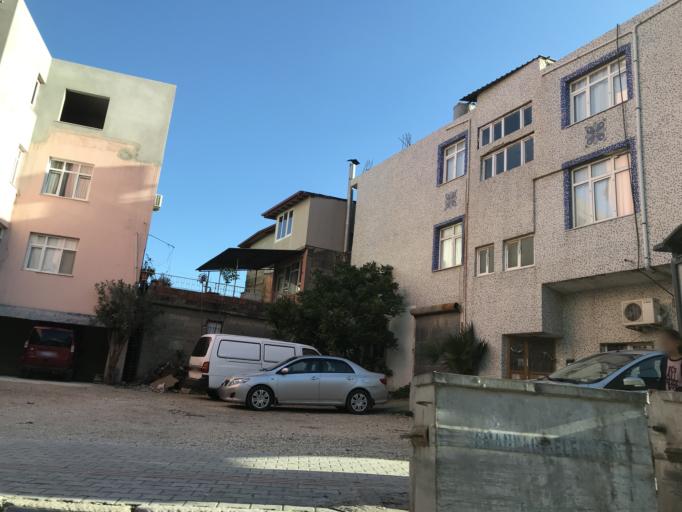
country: TR
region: Hatay
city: Samandag
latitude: 36.0847
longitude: 35.9736
